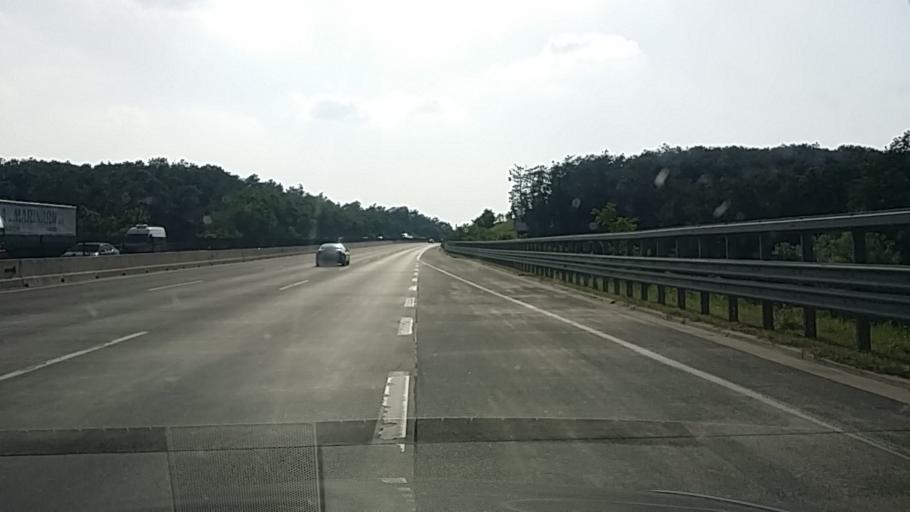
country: HU
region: Pest
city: Toeroekbalint
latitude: 47.4210
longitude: 18.9164
